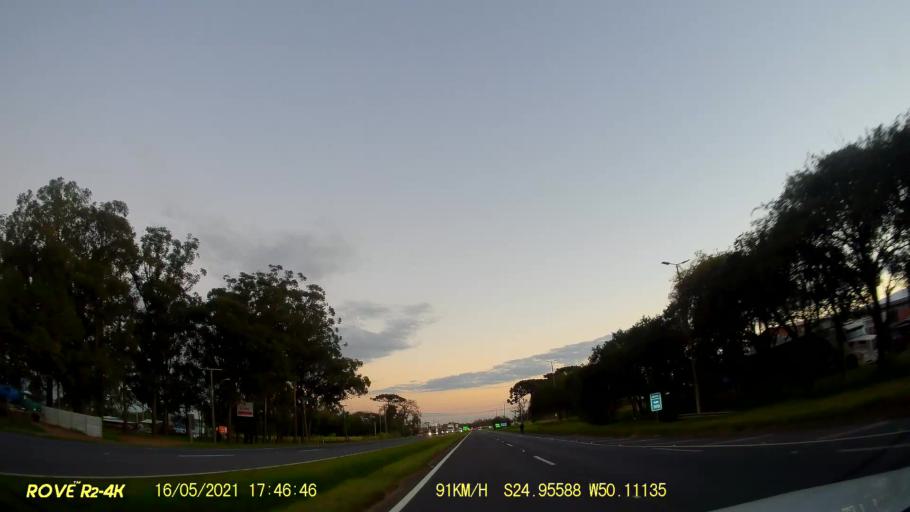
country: BR
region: Parana
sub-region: Carambei
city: Carambei
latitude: -24.9560
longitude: -50.1114
